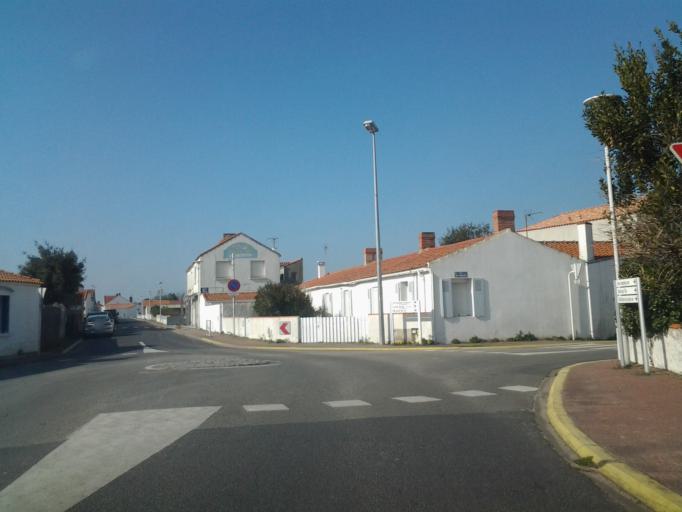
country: FR
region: Pays de la Loire
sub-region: Departement de la Vendee
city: La Gueriniere
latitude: 46.9683
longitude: -2.2289
